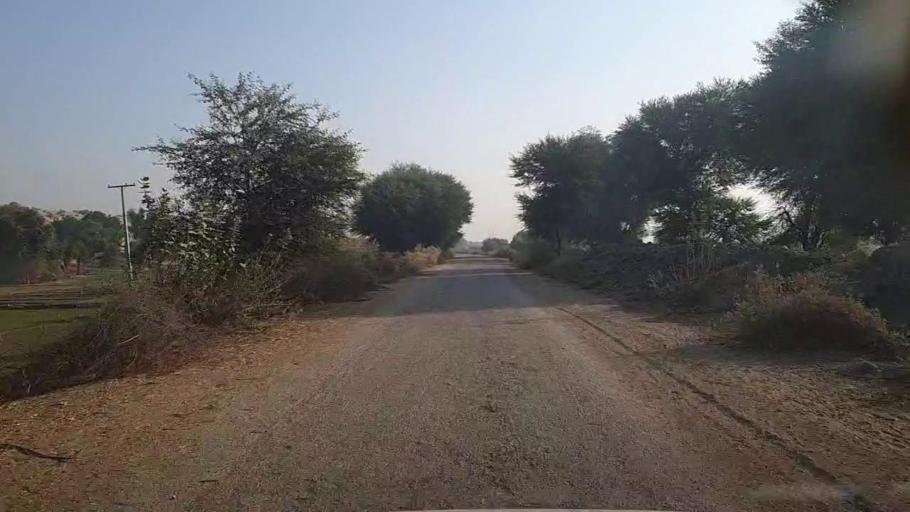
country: PK
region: Sindh
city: Karaundi
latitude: 26.7646
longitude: 68.4748
